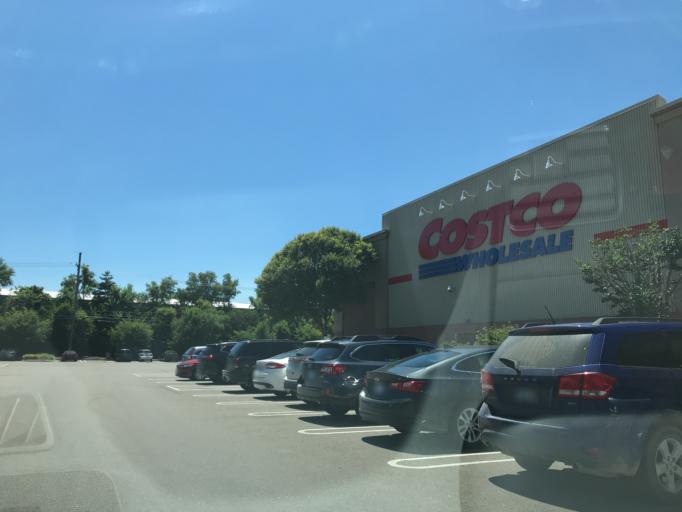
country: US
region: Michigan
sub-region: Livingston County
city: Brighton
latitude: 42.5030
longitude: -83.7615
